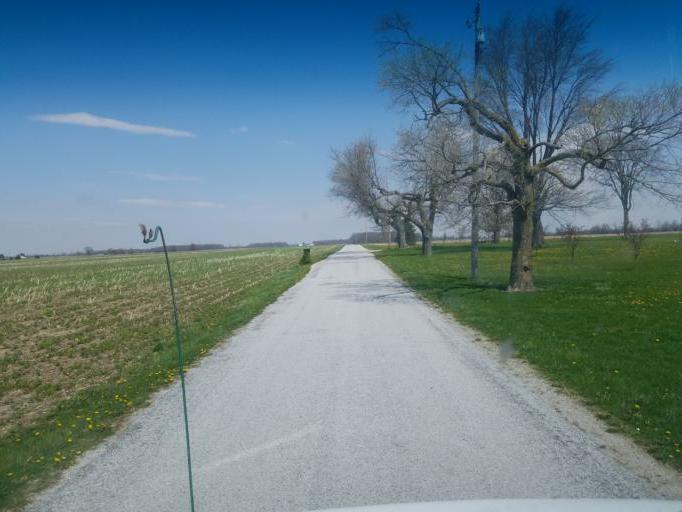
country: US
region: Ohio
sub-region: Hardin County
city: Kenton
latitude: 40.6968
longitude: -83.5473
